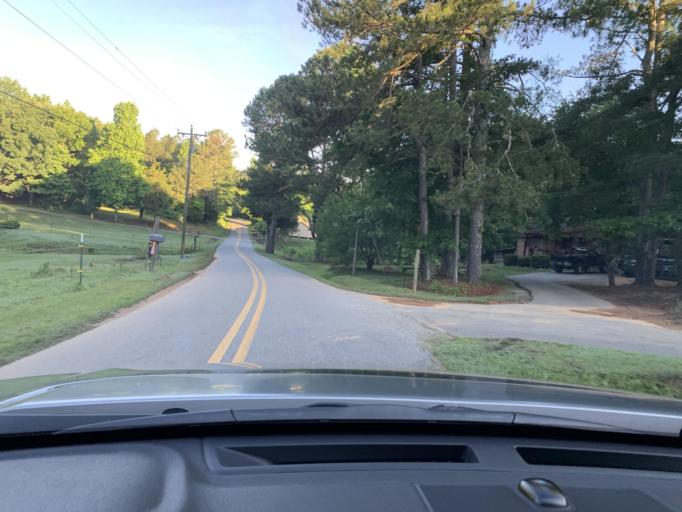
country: US
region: Georgia
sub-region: Bartow County
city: Rydal
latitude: 34.2500
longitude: -84.6799
